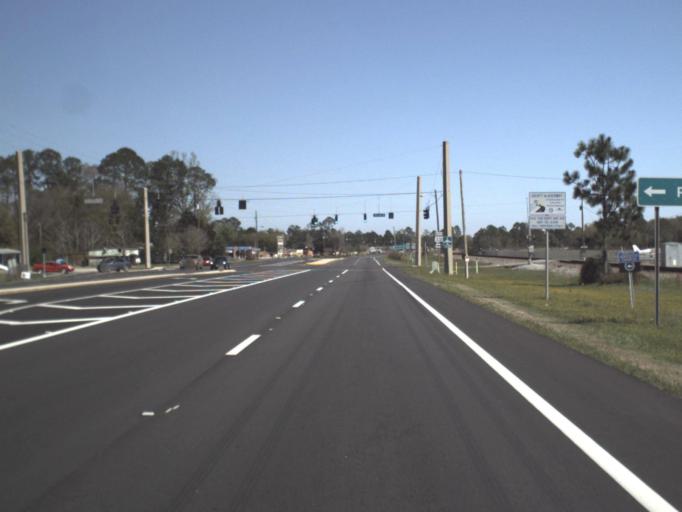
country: US
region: Florida
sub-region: Walton County
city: DeFuniak Springs
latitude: 30.7342
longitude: -86.1498
